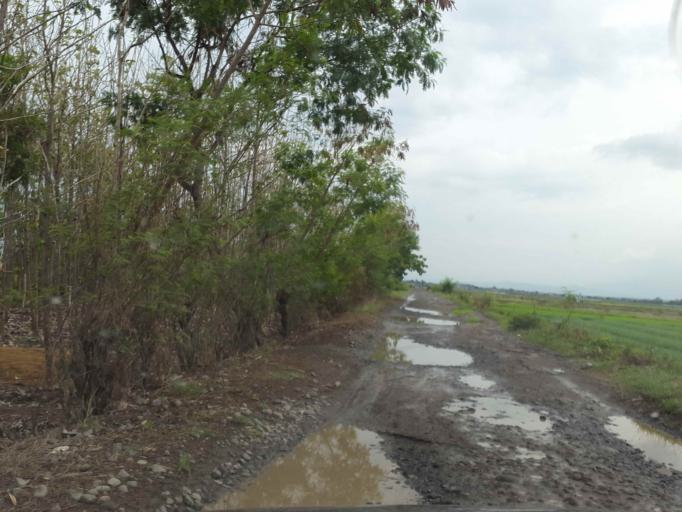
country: ID
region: Central Java
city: Ketanggungan
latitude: -6.9499
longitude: 108.9452
